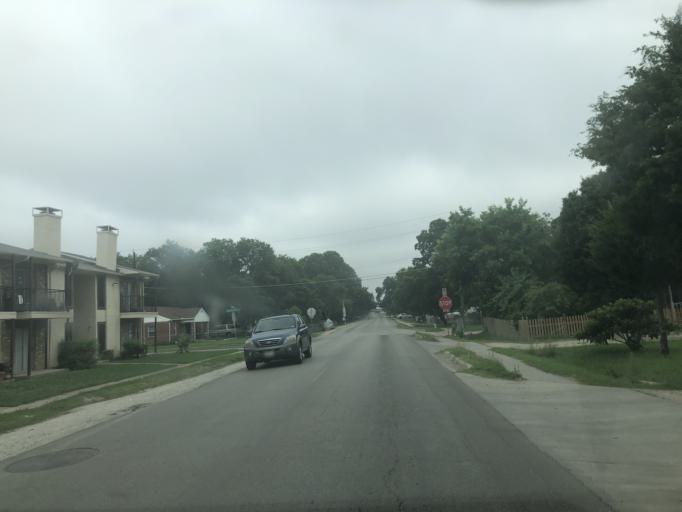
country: US
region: Texas
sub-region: Dallas County
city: University Park
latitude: 32.8614
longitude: -96.8696
